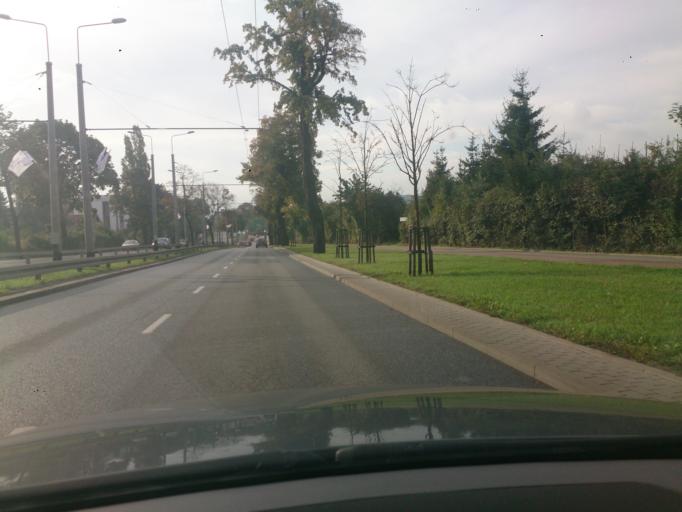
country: PL
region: Pomeranian Voivodeship
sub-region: Gdynia
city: Gdynia
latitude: 54.4901
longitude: 18.5420
